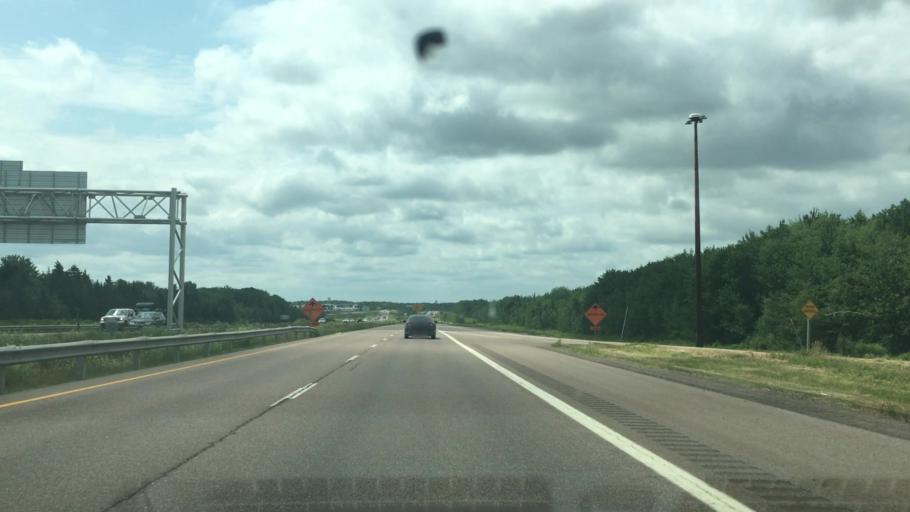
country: CA
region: New Brunswick
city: Dieppe
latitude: 46.1242
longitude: -64.6864
